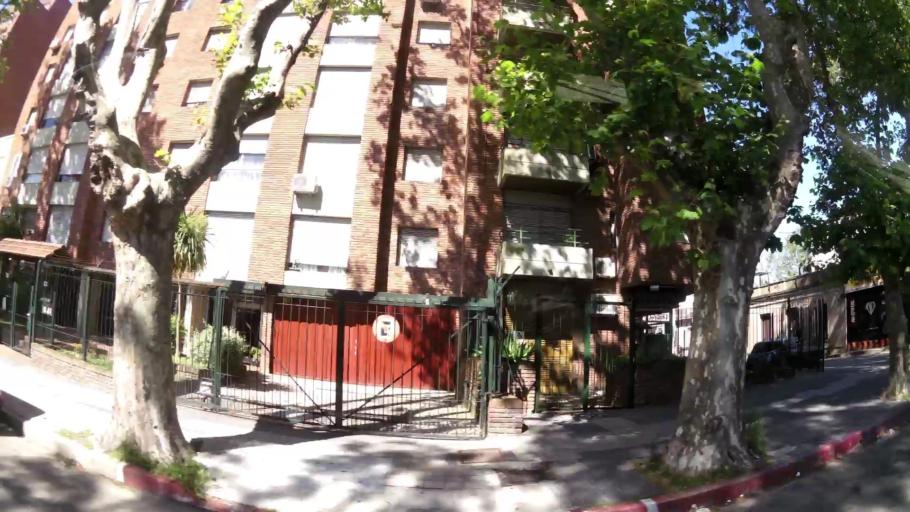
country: UY
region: Montevideo
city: Montevideo
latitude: -34.8897
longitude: -56.1272
